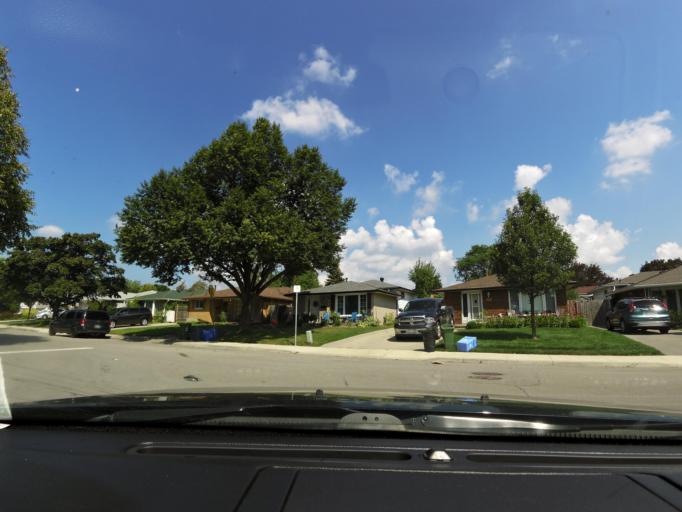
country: CA
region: Ontario
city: Hamilton
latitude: 43.2181
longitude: -79.9133
